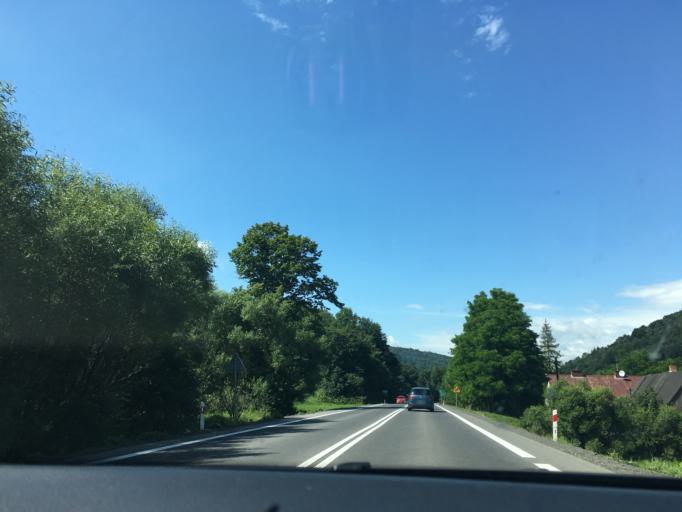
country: PL
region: Subcarpathian Voivodeship
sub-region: Powiat krosnienski
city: Dukla
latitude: 49.5138
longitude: 21.6944
